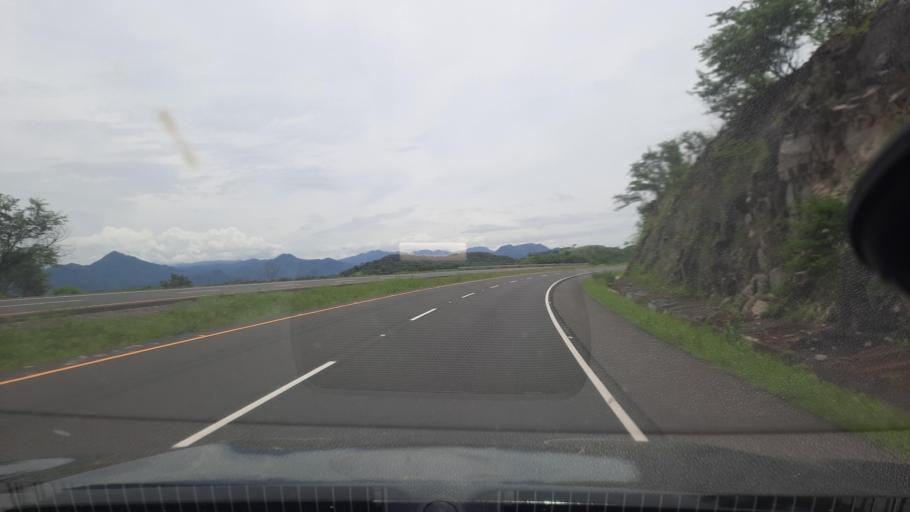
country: HN
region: Valle
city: Aramecina
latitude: 13.7366
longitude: -87.7201
